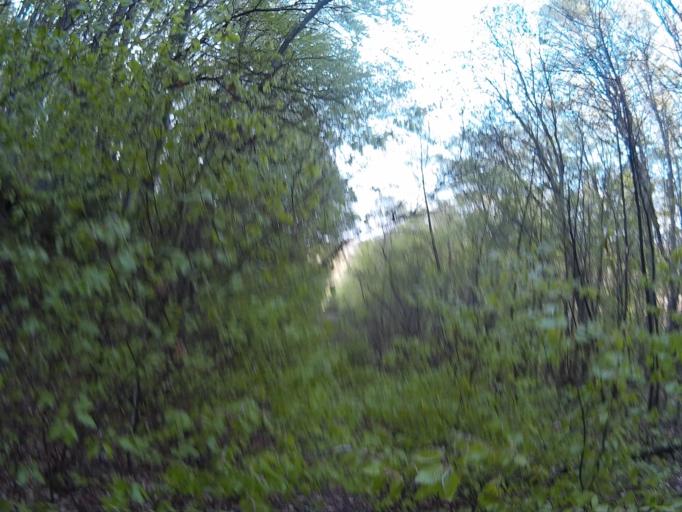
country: AT
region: Burgenland
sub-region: Politischer Bezirk Oberwart
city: Rechnitz
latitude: 47.3362
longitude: 16.4723
